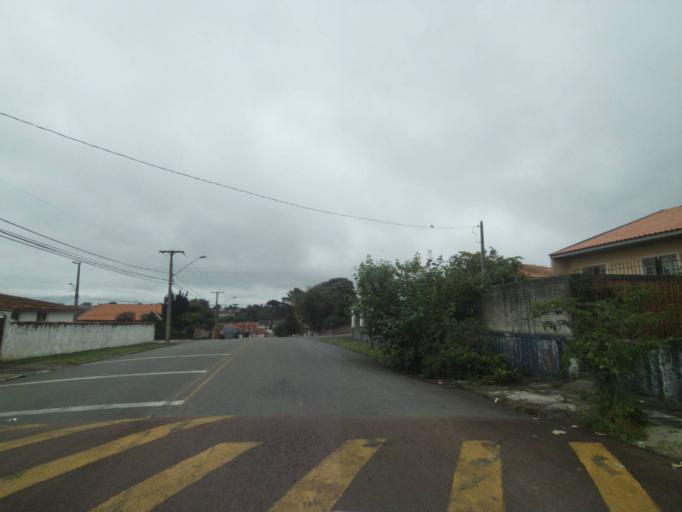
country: BR
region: Parana
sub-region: Curitiba
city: Curitiba
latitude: -25.4255
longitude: -49.3437
